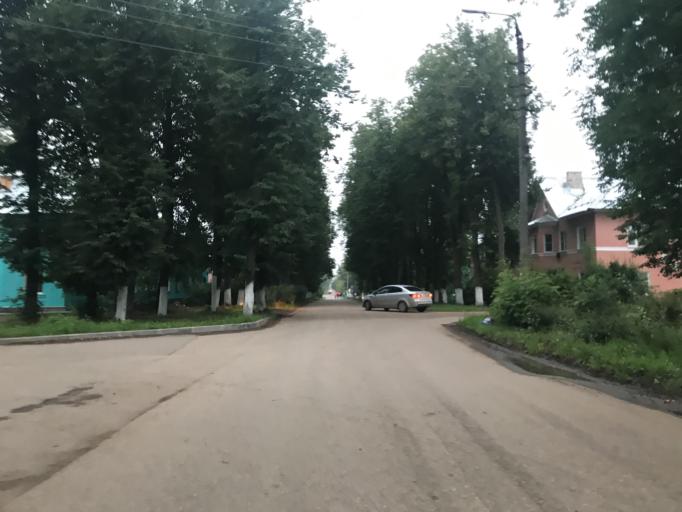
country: RU
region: Tula
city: Priupskiy
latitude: 53.9445
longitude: 37.7014
